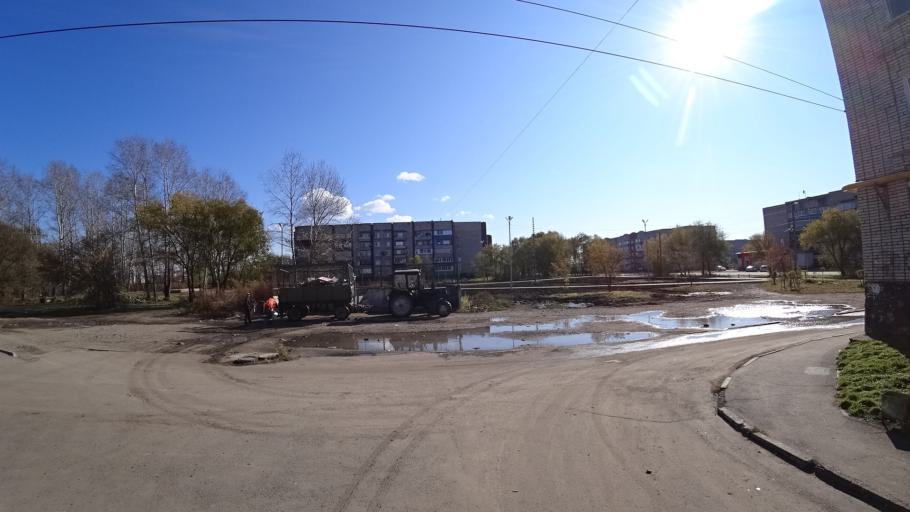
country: RU
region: Khabarovsk Krai
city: Amursk
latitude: 50.1003
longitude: 136.5148
